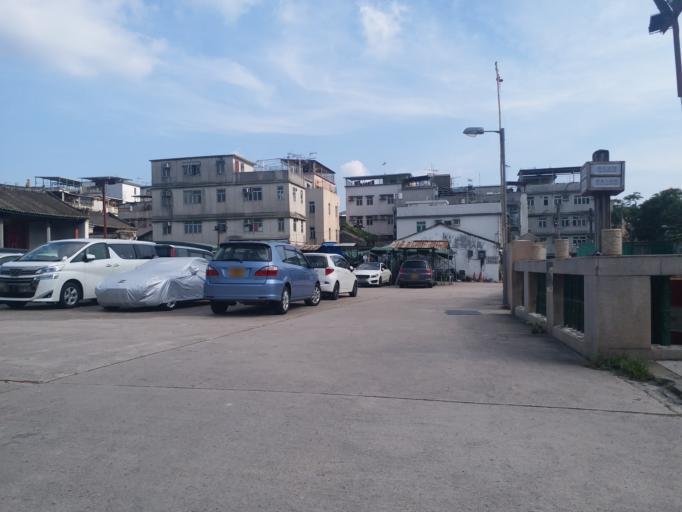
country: HK
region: Yuen Long
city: Yuen Long Kau Hui
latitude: 22.4454
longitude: 114.0077
